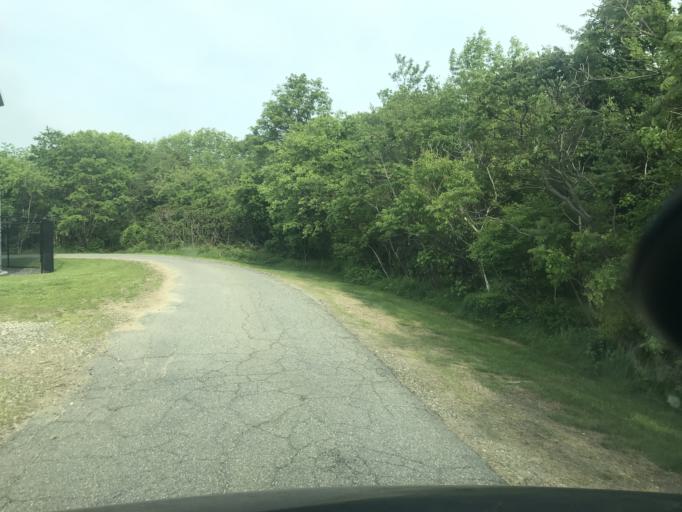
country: US
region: Massachusetts
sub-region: Essex County
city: Rockport
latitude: 42.6724
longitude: -70.6287
